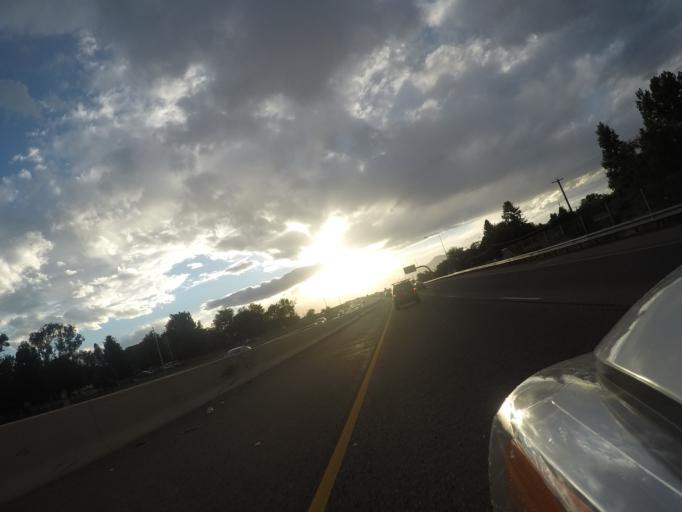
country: US
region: Colorado
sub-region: Arapahoe County
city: Sheridan
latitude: 39.6529
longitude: -105.0753
